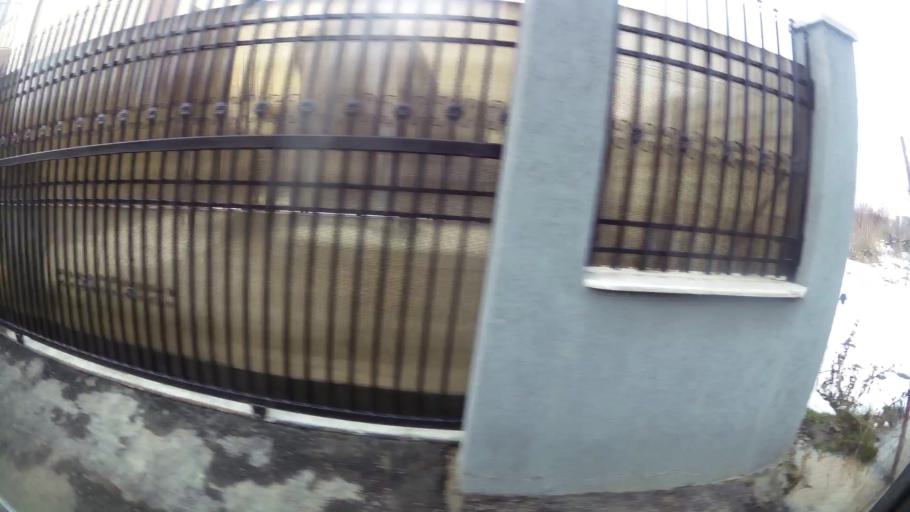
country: RO
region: Ilfov
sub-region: Comuna Popesti-Leordeni
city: Popesti-Leordeni
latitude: 44.4016
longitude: 26.1813
